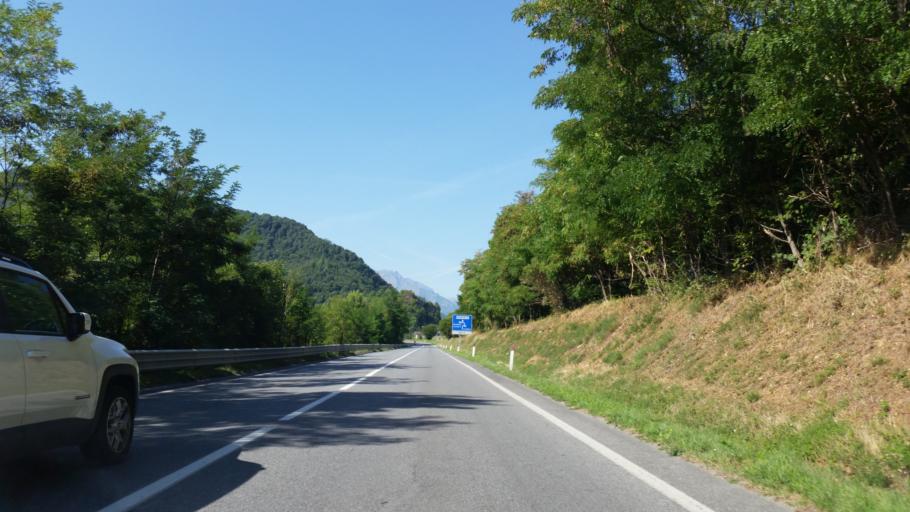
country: IT
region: Piedmont
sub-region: Provincia di Cuneo
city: Roccavione
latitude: 44.3194
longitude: 7.4917
